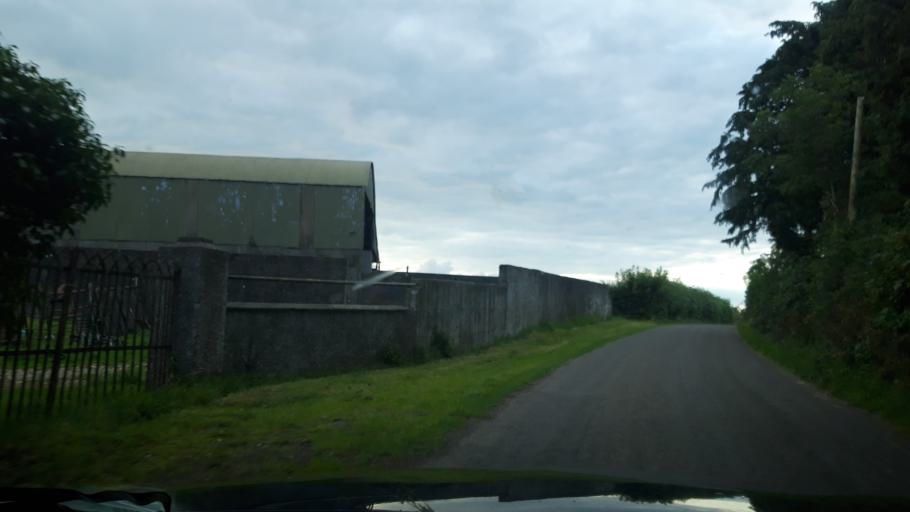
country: IE
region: Leinster
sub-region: Kilkenny
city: Graiguenamanagh
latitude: 52.5691
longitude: -6.9803
